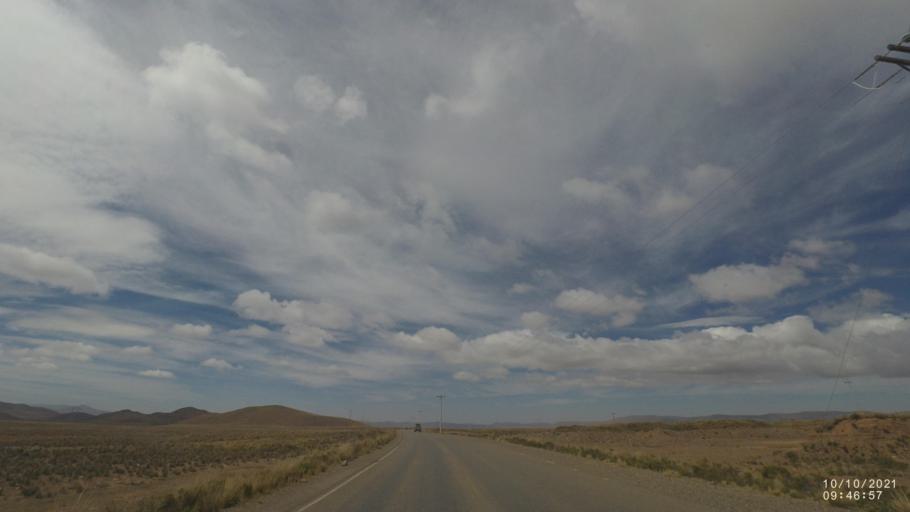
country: BO
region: La Paz
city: Quime
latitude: -17.1868
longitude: -67.3405
